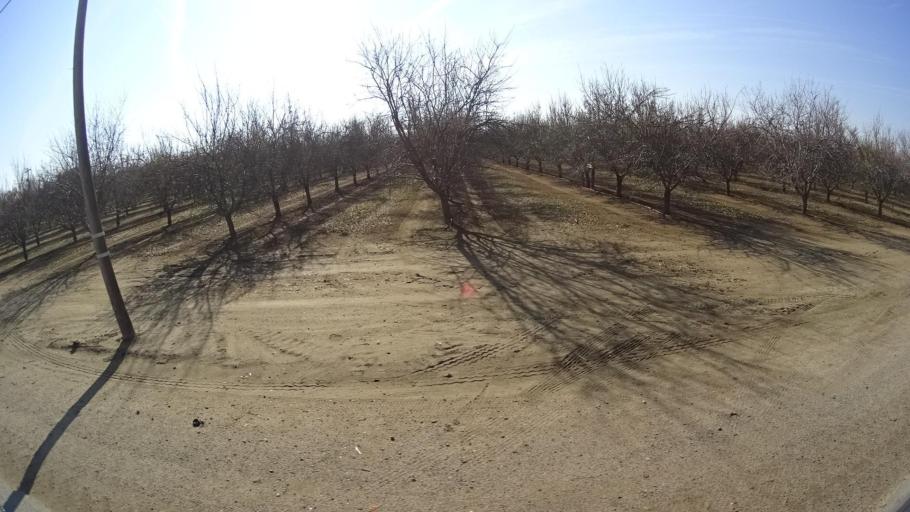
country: US
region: California
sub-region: Kern County
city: Weedpatch
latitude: 35.2379
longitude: -118.9016
